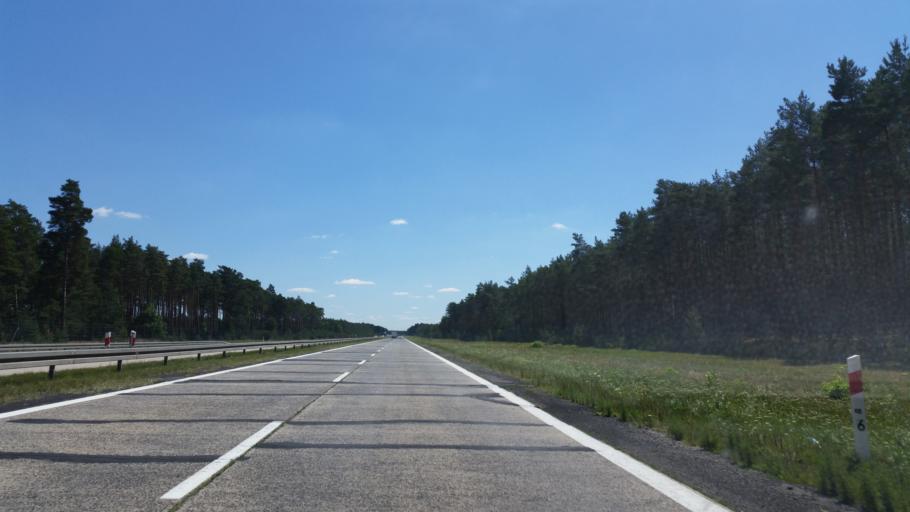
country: PL
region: Lower Silesian Voivodeship
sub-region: Powiat boleslawiecki
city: Boleslawiec
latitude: 51.3888
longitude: 15.5378
